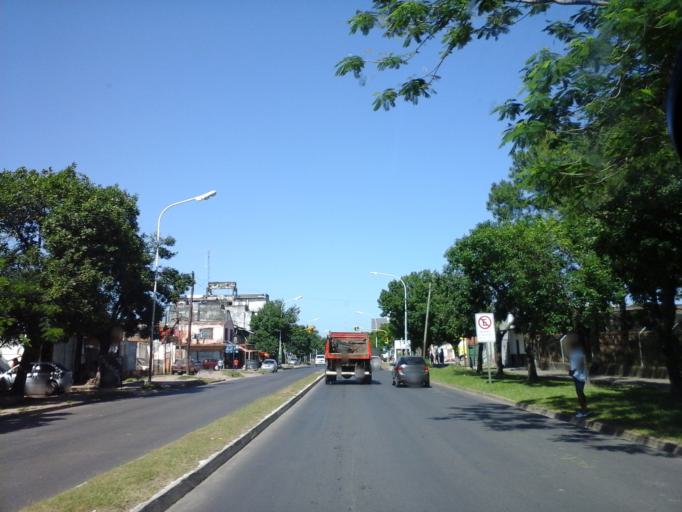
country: AR
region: Corrientes
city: Corrientes
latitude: -27.4683
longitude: -58.7965
